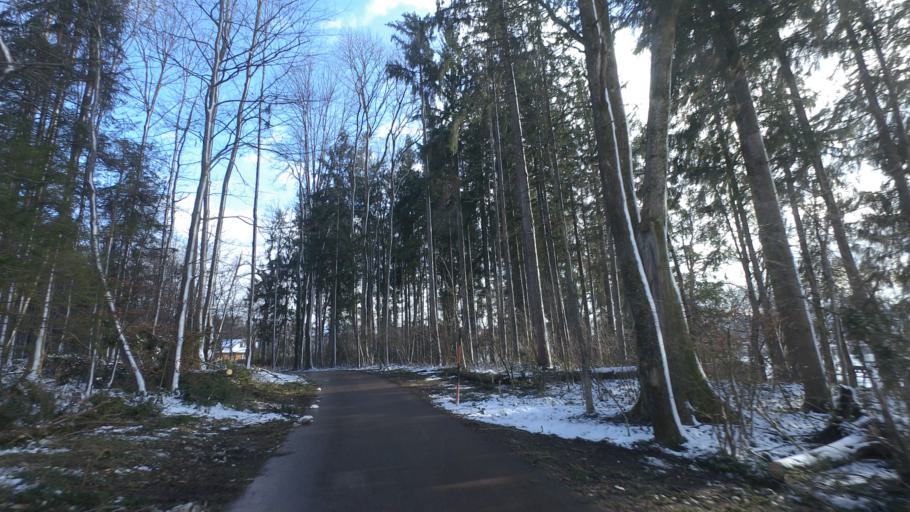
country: DE
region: Bavaria
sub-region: Upper Bavaria
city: Traunstein
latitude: 47.8826
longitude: 12.6237
